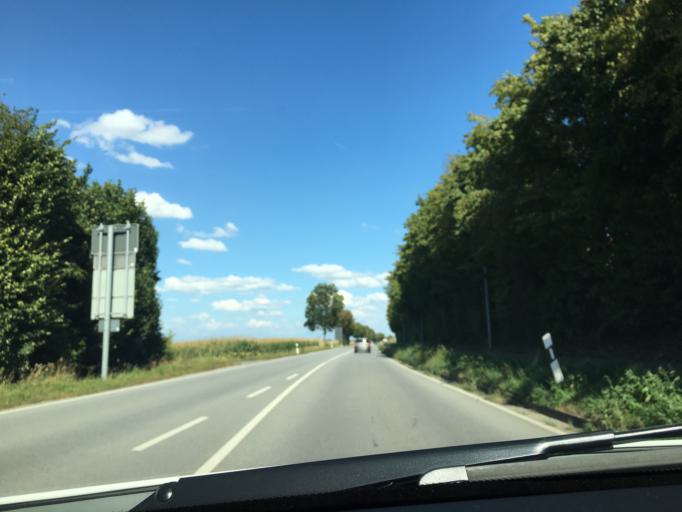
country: DE
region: Bavaria
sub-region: Lower Bavaria
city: Dingolfing
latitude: 48.6486
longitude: 12.5047
